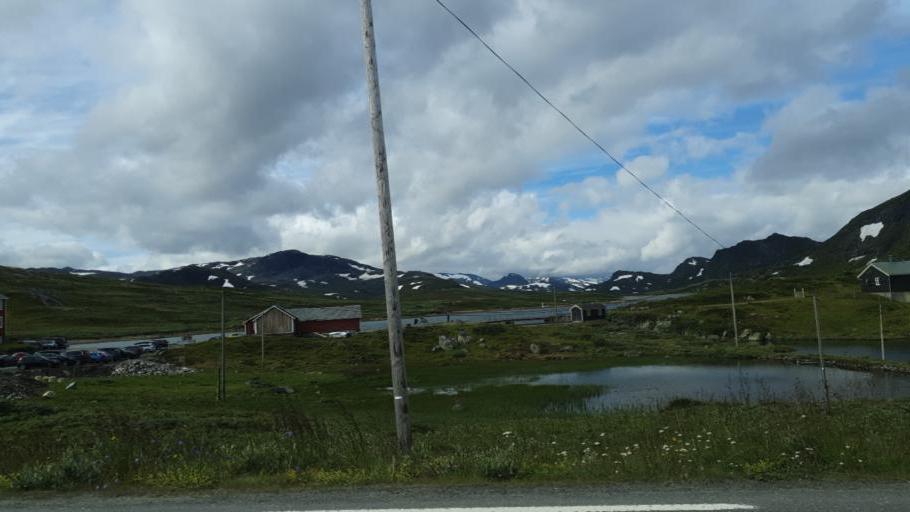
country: NO
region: Oppland
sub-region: Vestre Slidre
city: Slidre
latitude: 61.3287
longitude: 8.7995
